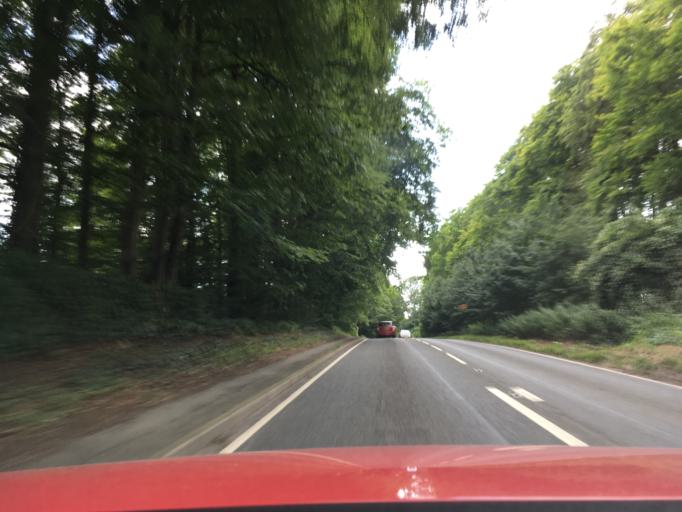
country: GB
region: England
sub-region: Hampshire
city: Compton
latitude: 51.0332
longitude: -1.3295
